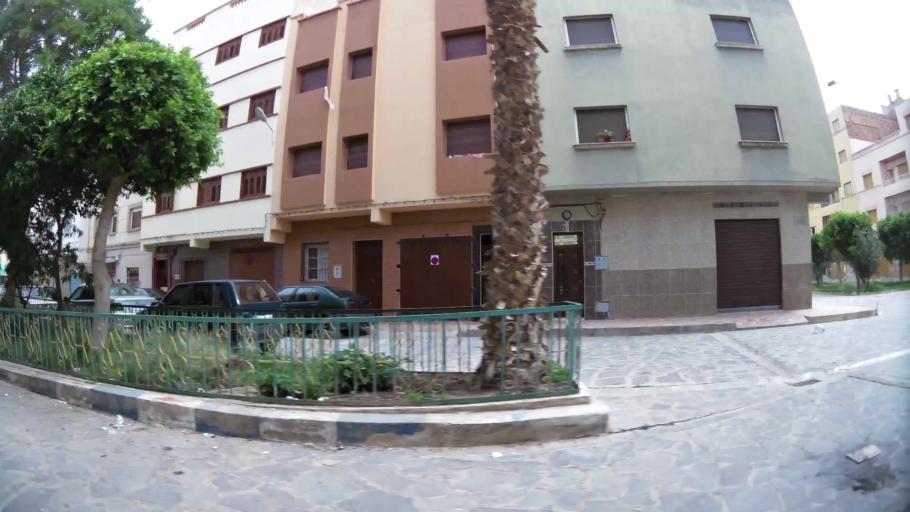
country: MA
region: Oriental
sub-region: Nador
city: Nador
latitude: 35.1736
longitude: -2.9311
